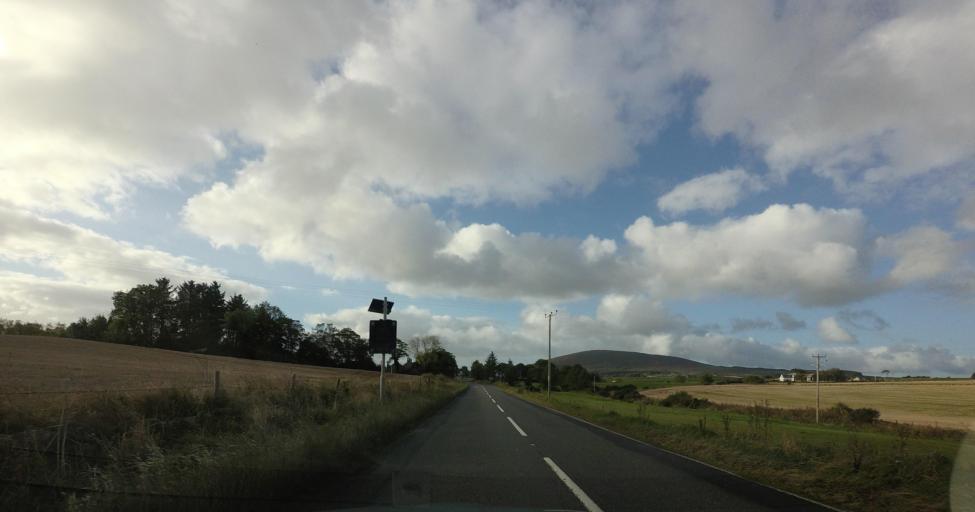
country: GB
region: Scotland
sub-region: Aberdeenshire
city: Portsoy
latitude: 57.5998
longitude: -2.7254
